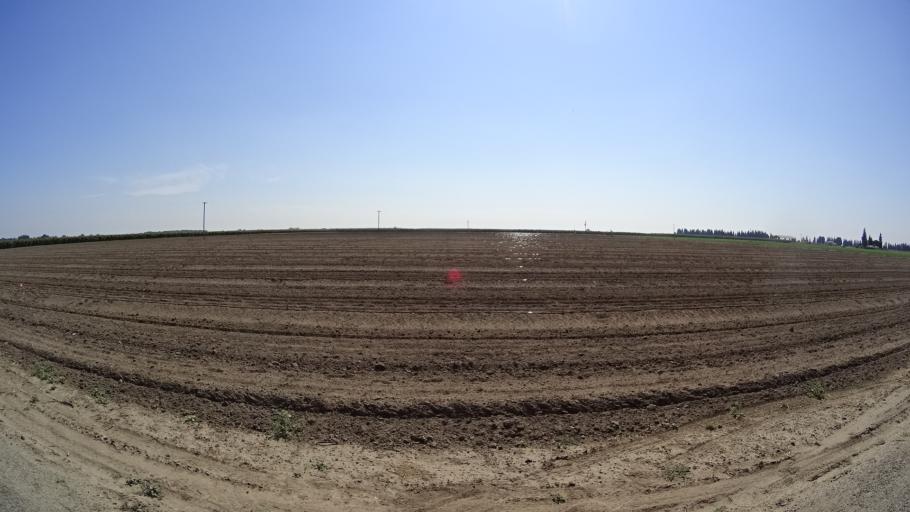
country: US
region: California
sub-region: Kings County
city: Lucerne
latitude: 36.4215
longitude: -119.5829
